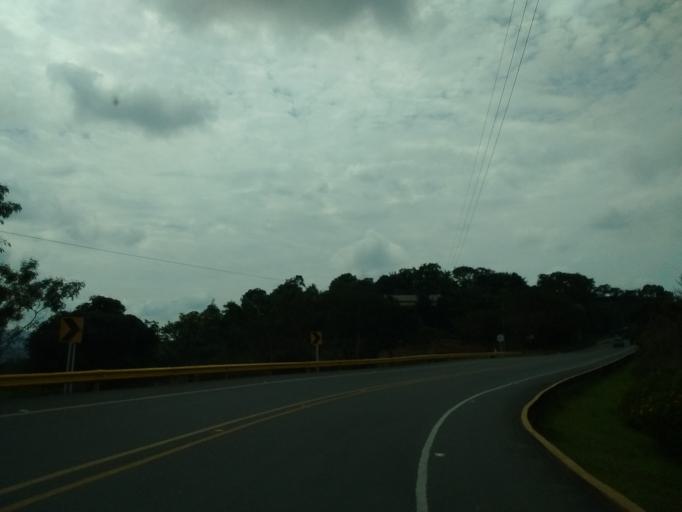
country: CO
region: Cauca
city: Morales
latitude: 2.7765
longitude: -76.5539
